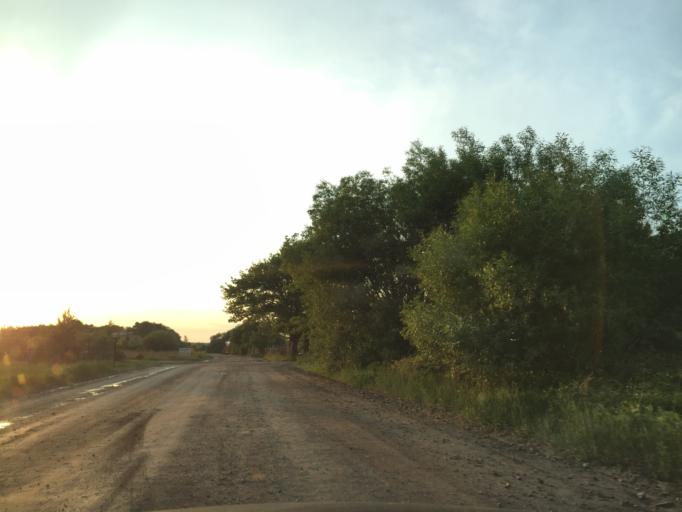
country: LT
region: Klaipedos apskritis
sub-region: Klaipeda
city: Klaipeda
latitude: 55.7545
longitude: 21.1527
